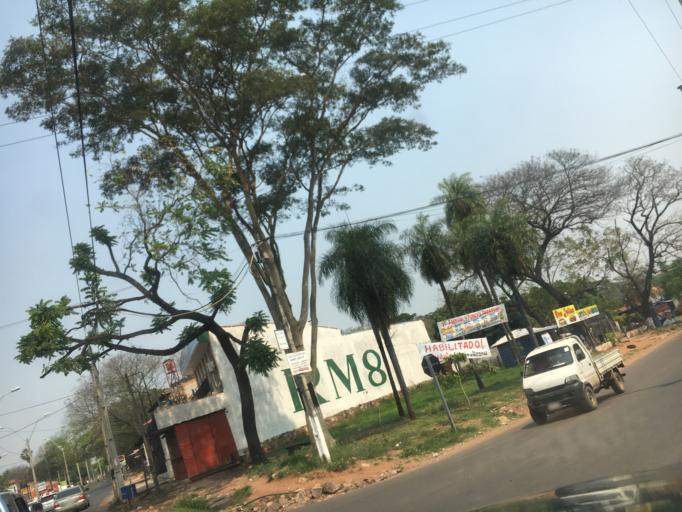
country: PY
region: Central
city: Villa Elisa
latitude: -25.3705
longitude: -57.5843
